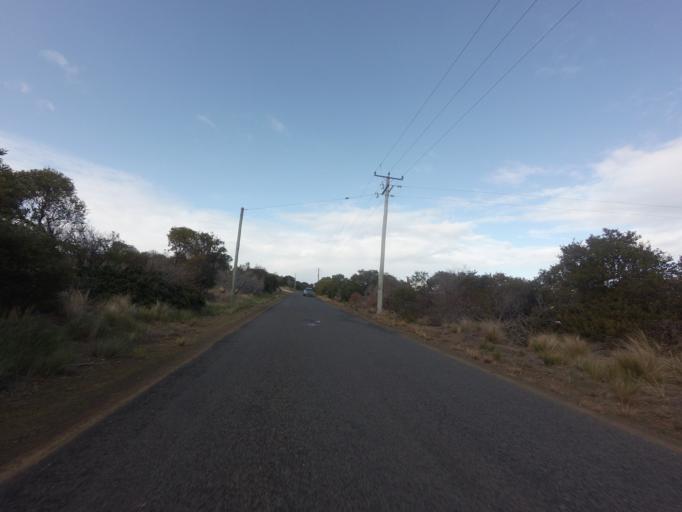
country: AU
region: Tasmania
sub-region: Break O'Day
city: St Helens
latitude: -42.0883
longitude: 148.1434
